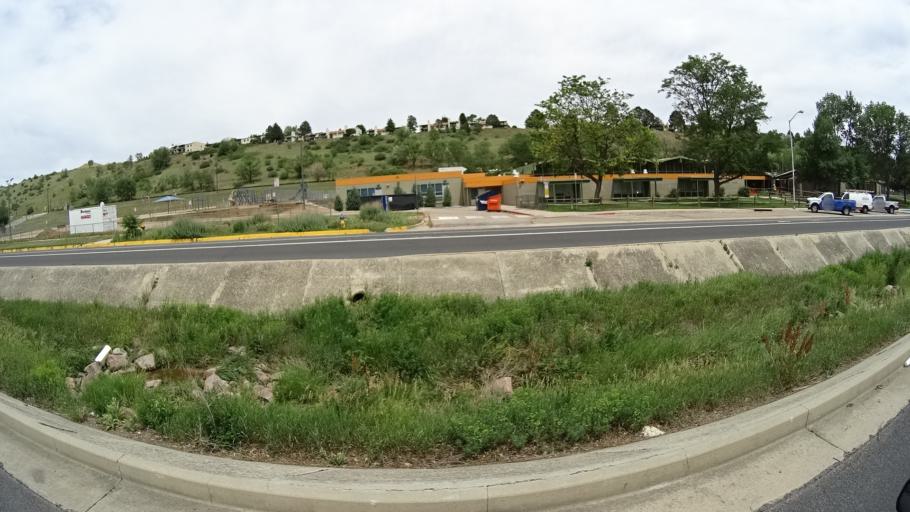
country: US
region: Colorado
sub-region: El Paso County
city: Manitou Springs
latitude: 38.8658
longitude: -104.8683
